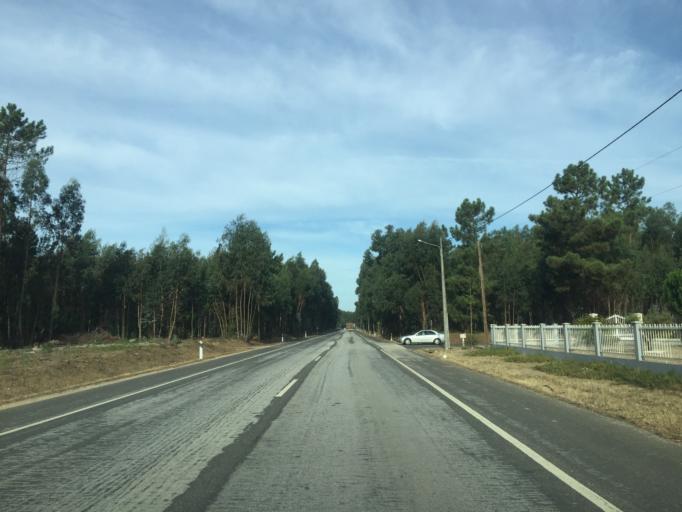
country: PT
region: Coimbra
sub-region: Figueira da Foz
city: Lavos
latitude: 40.0321
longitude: -8.8394
